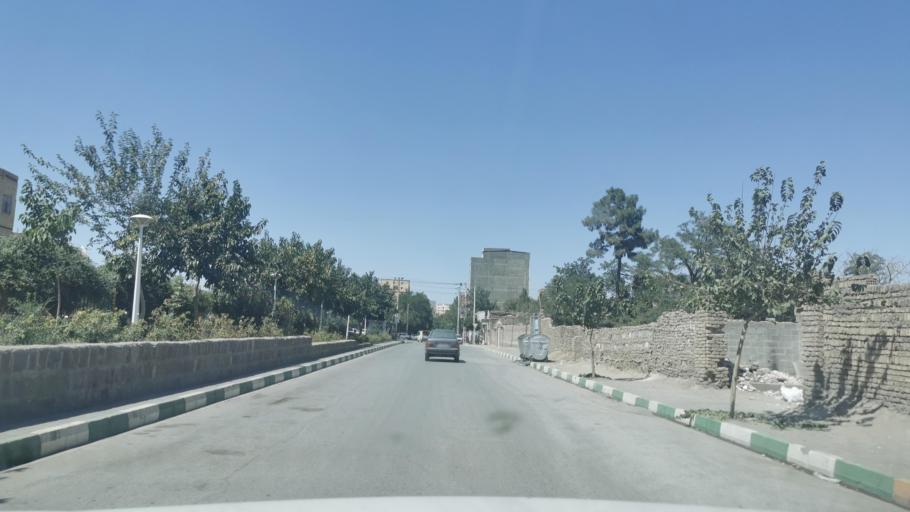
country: IR
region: Razavi Khorasan
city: Mashhad
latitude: 36.3607
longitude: 59.5592
